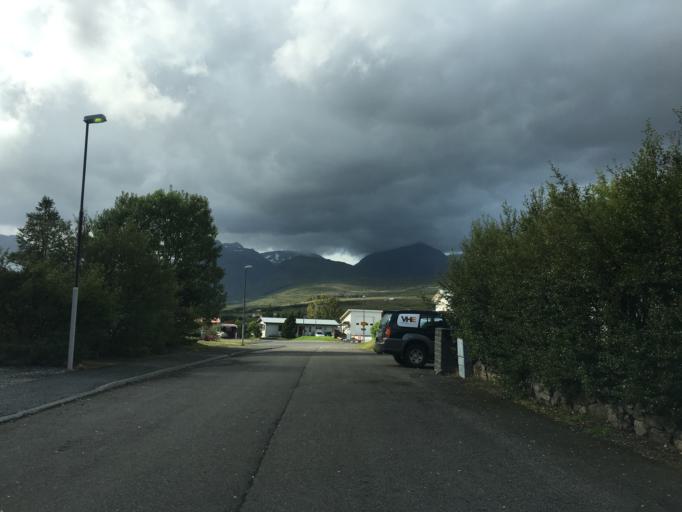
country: IS
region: East
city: Reydarfjoerdur
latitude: 65.0363
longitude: -14.2083
